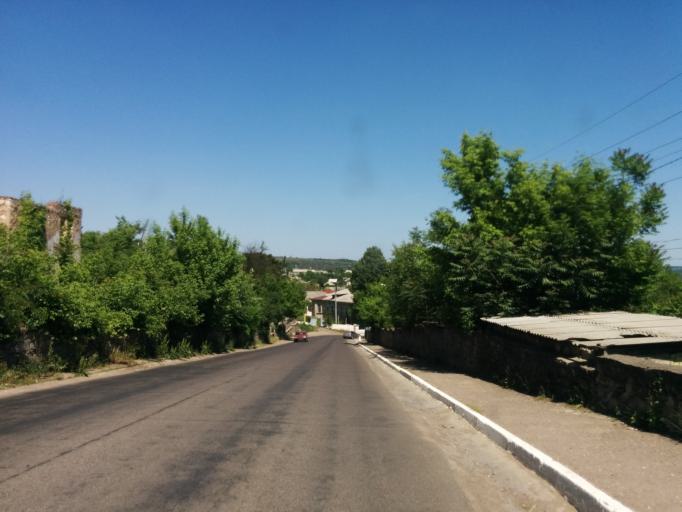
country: MD
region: Raionul Soroca
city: Soroca
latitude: 48.1616
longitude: 28.2969
